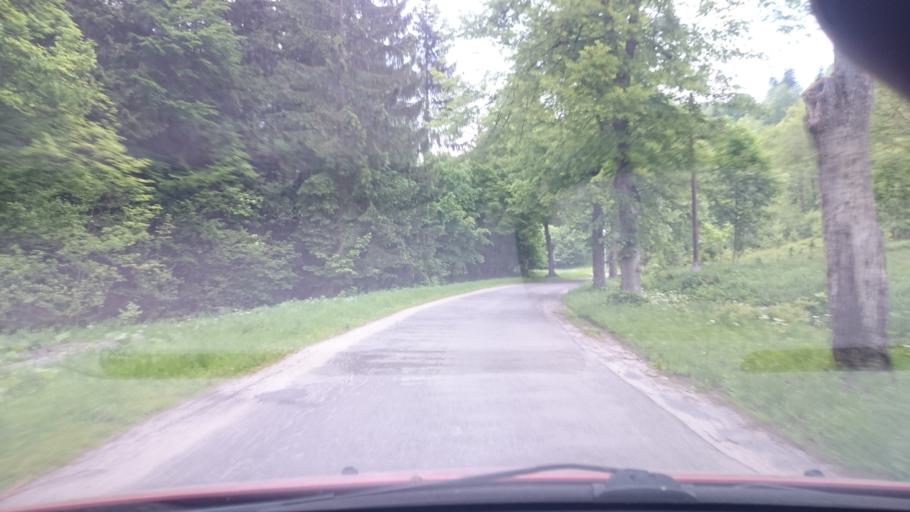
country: PL
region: Lower Silesian Voivodeship
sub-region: Powiat klodzki
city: Polanica-Zdroj
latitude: 50.3030
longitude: 16.5327
